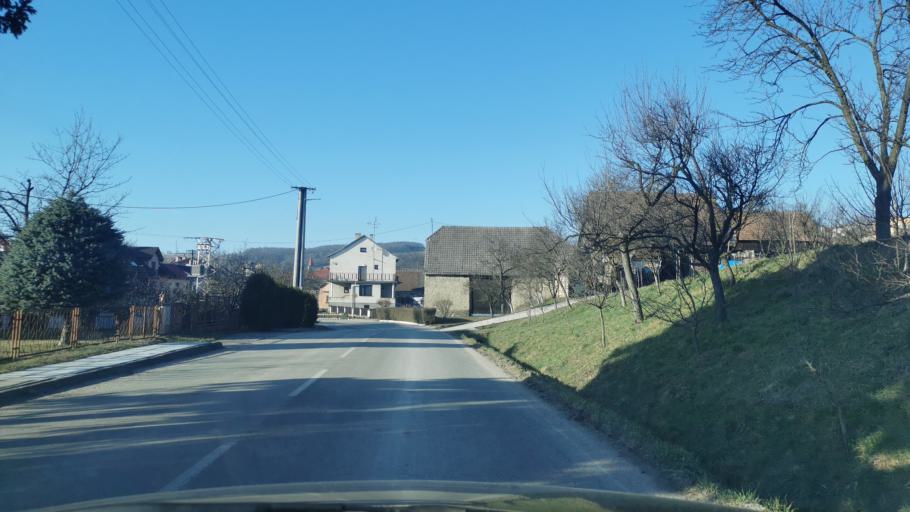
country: SK
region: Trnavsky
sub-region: Okres Senica
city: Senica
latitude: 48.7436
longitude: 17.3553
